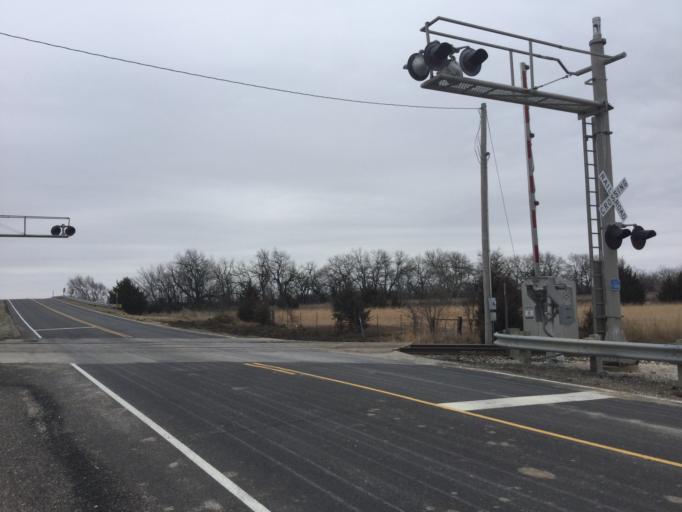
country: US
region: Kansas
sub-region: Sumner County
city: Mulvane
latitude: 37.5191
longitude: -97.2048
